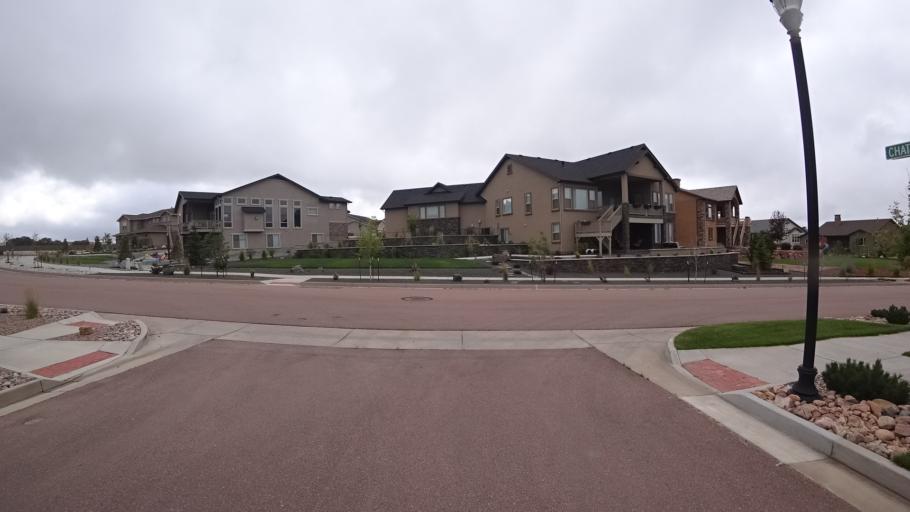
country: US
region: Colorado
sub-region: El Paso County
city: Gleneagle
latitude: 39.0129
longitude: -104.7875
